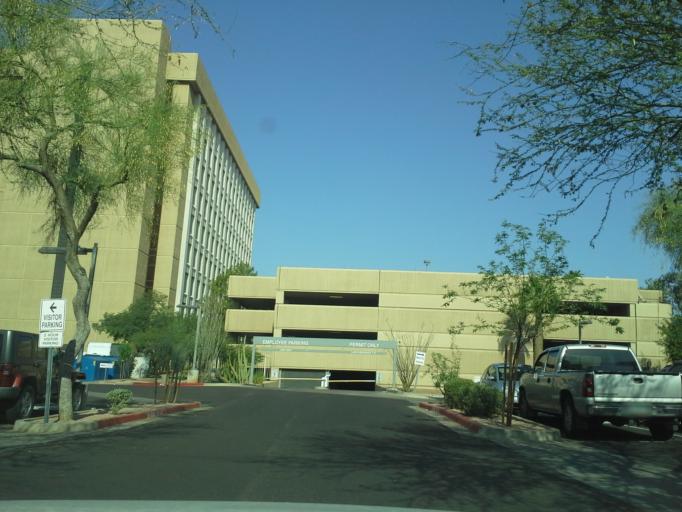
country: US
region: Arizona
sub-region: Maricopa County
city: Phoenix
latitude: 33.4509
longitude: -112.0938
